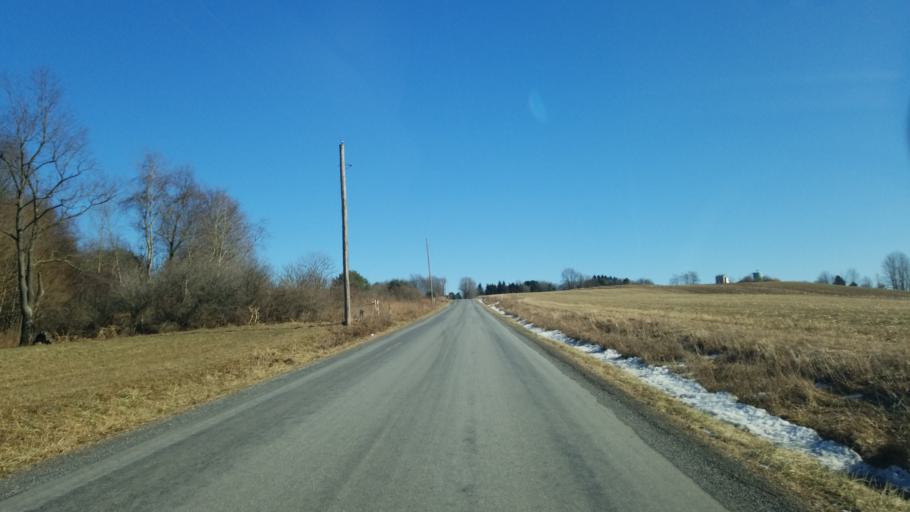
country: US
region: Pennsylvania
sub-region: Jefferson County
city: Sykesville
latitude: 41.0367
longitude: -78.7792
